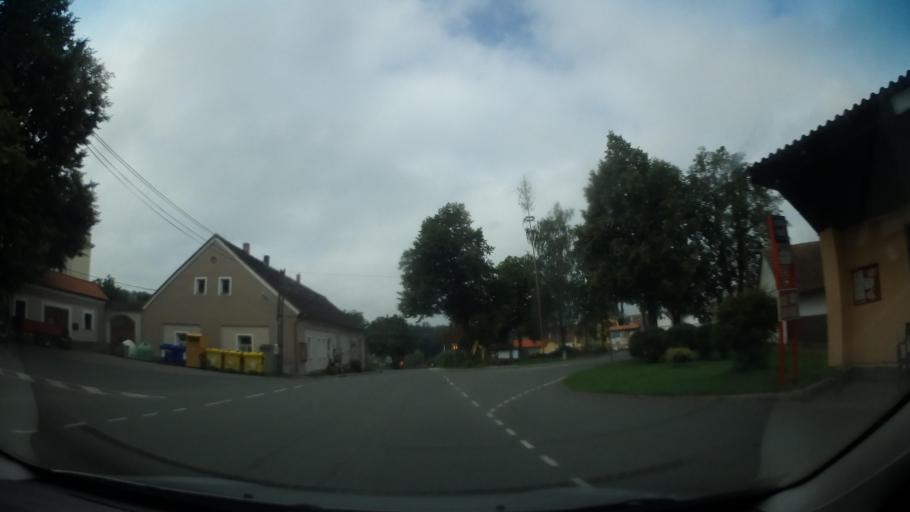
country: CZ
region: Central Bohemia
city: Neveklov
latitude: 49.7215
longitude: 14.4770
